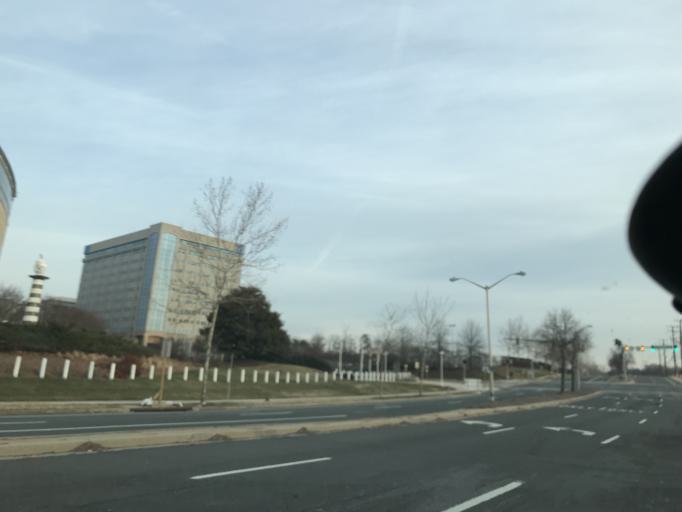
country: US
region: Maryland
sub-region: Prince George's County
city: Woodlawn
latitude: 38.9490
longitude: -76.8727
